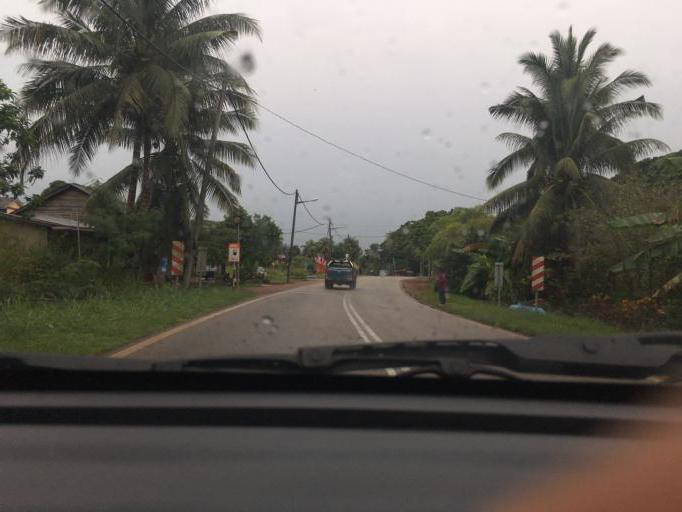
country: MY
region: Kedah
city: Bedong
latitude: 5.6932
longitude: 100.6319
